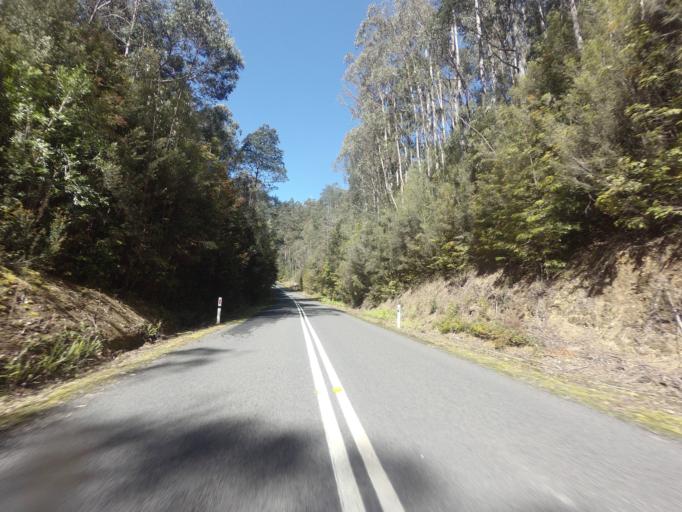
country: AU
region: Tasmania
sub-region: Huon Valley
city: Geeveston
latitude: -42.8203
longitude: 146.2910
